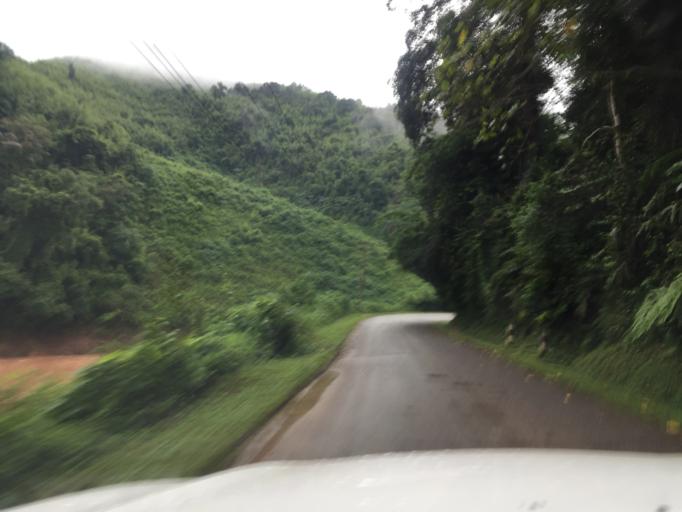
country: LA
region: Oudomxai
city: Muang La
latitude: 20.9203
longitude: 102.2021
